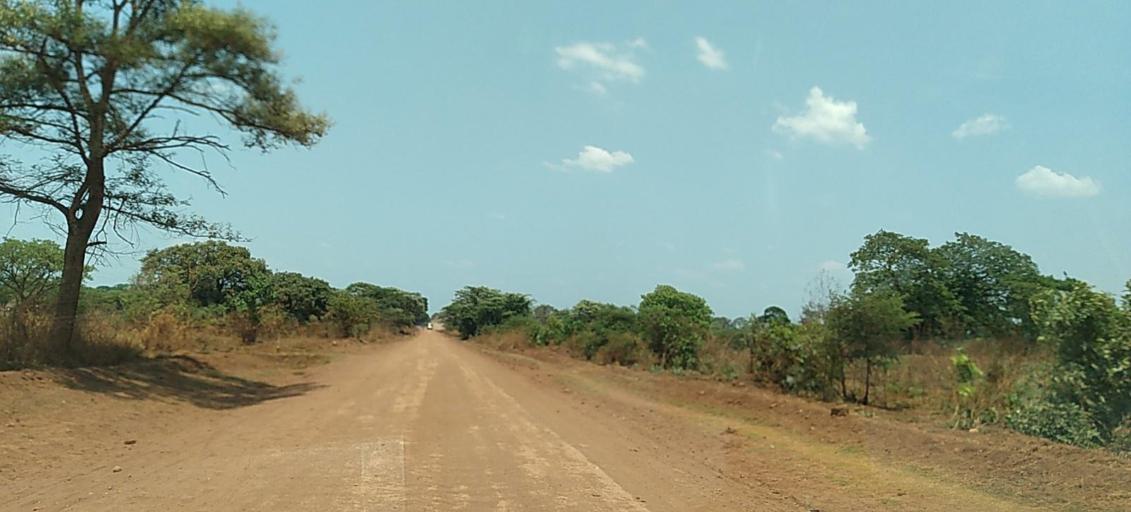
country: ZM
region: Copperbelt
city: Mpongwe
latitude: -13.5140
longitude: 28.0299
